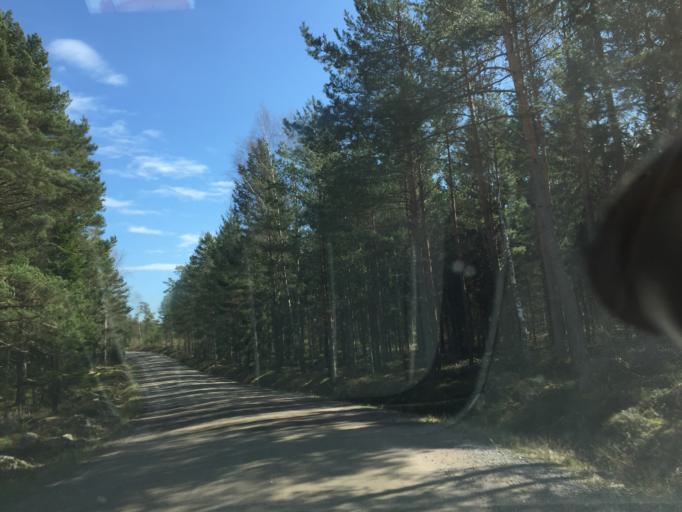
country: FI
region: Uusimaa
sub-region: Raaseporin
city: Hanko
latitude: 59.9431
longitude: 22.9357
